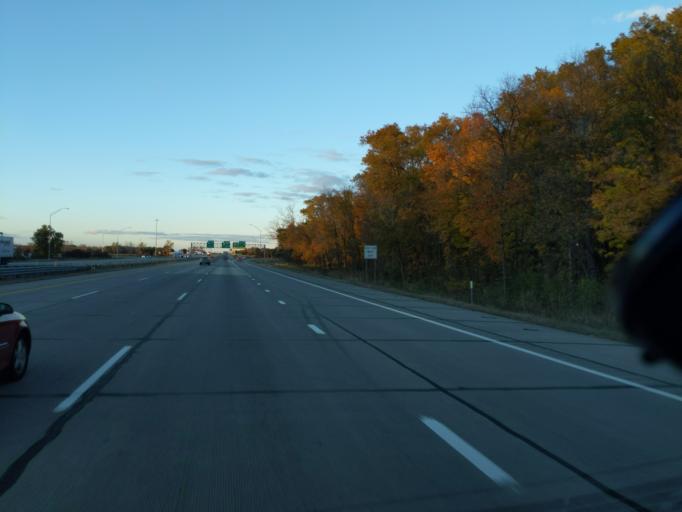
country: US
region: Michigan
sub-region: Eaton County
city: Waverly
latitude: 42.7337
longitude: -84.6682
